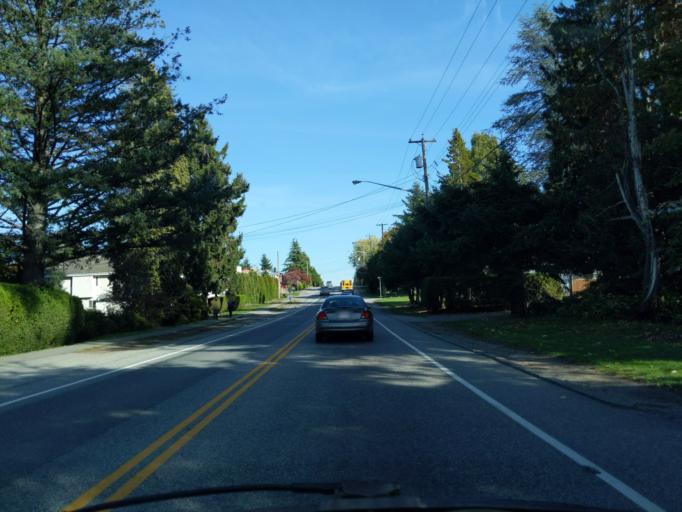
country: CA
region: British Columbia
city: New Westminster
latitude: 49.1917
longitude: -122.8725
